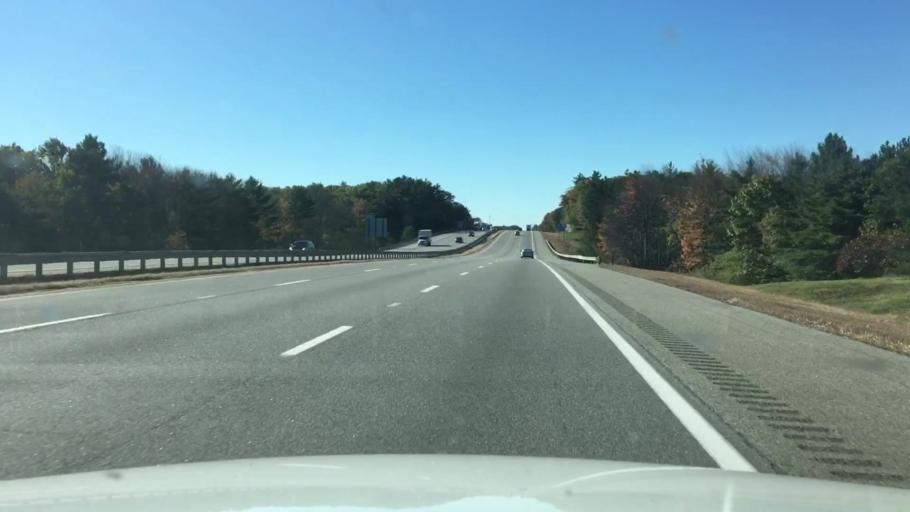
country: US
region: Maine
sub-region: York County
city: West Kennebunk
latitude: 43.3952
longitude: -70.5683
